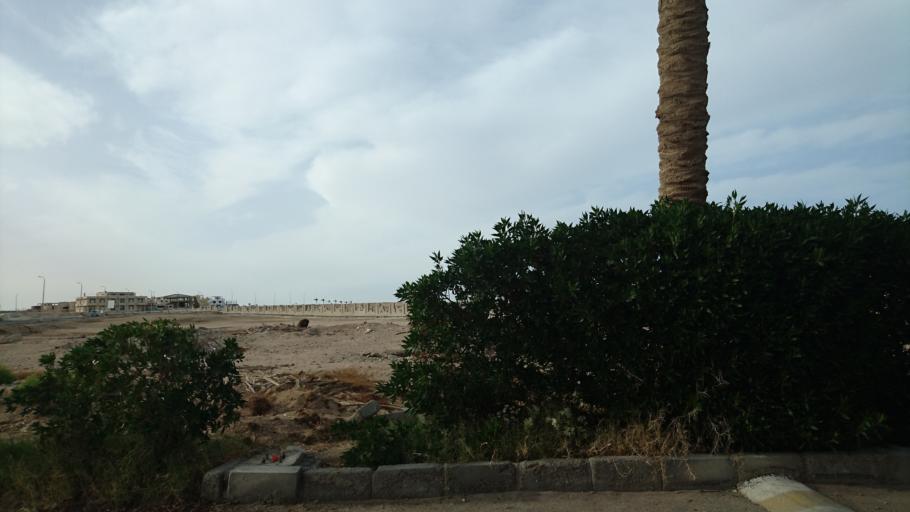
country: EG
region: Red Sea
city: Bur Safajah
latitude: 26.8010
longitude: 33.9394
